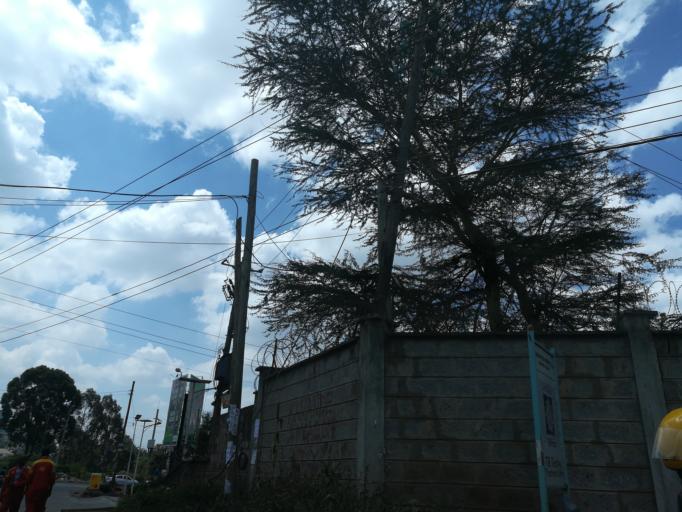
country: KE
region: Nairobi Area
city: Nairobi
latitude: -1.3077
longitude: 36.8032
